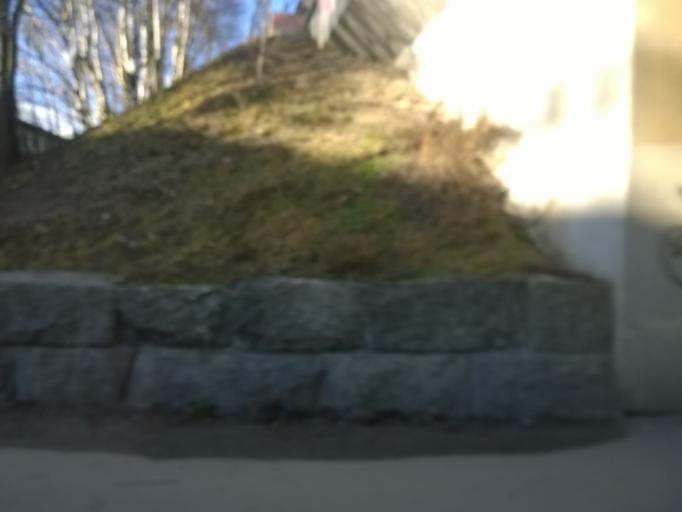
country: FI
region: Pirkanmaa
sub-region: Tampere
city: Tampere
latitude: 61.4911
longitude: 23.7733
